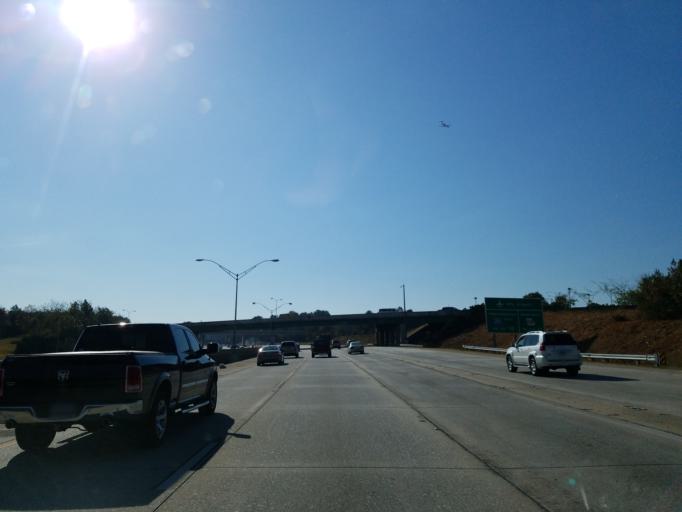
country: US
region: Georgia
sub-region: Fulton County
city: College Park
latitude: 33.6494
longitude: -84.4446
